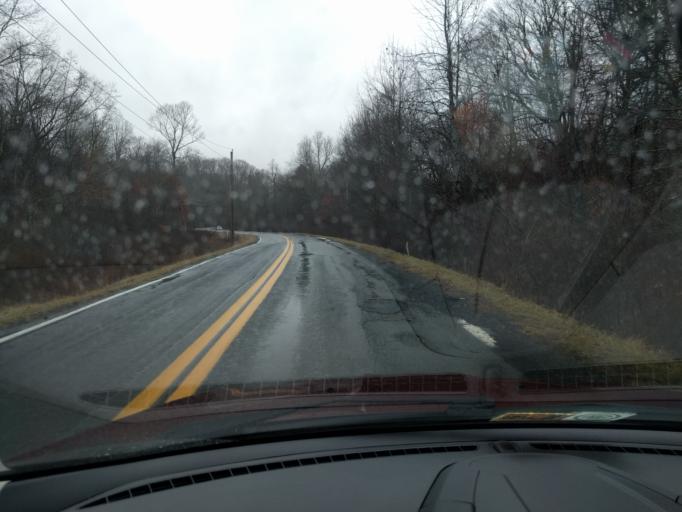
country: US
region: West Virginia
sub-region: Raleigh County
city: Beckley
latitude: 37.7951
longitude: -81.1975
